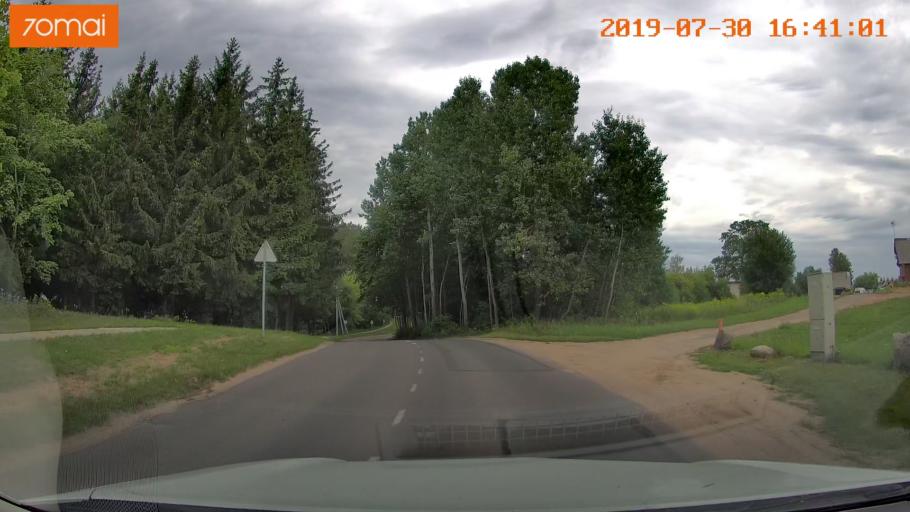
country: LT
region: Vilnius County
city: Rasos
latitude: 54.7083
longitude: 25.3584
